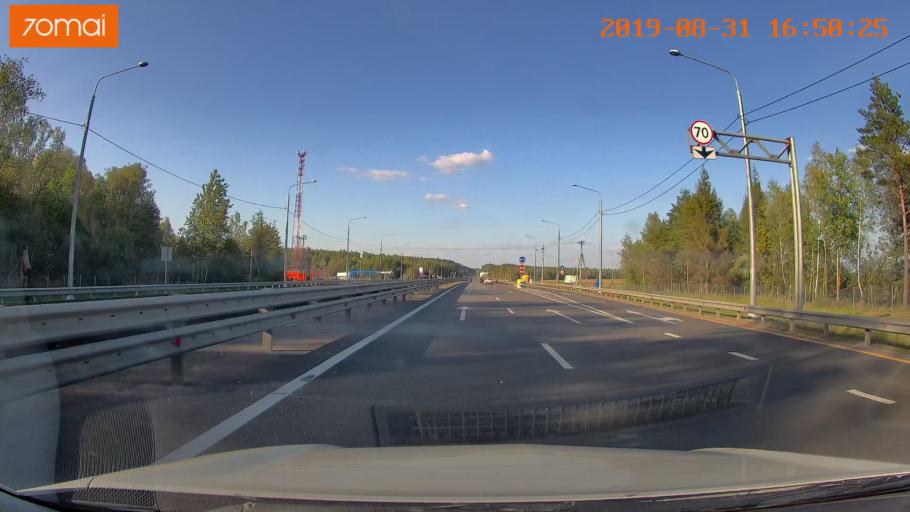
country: RU
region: Kaluga
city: Pyatovskiy
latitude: 54.7082
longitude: 36.1625
